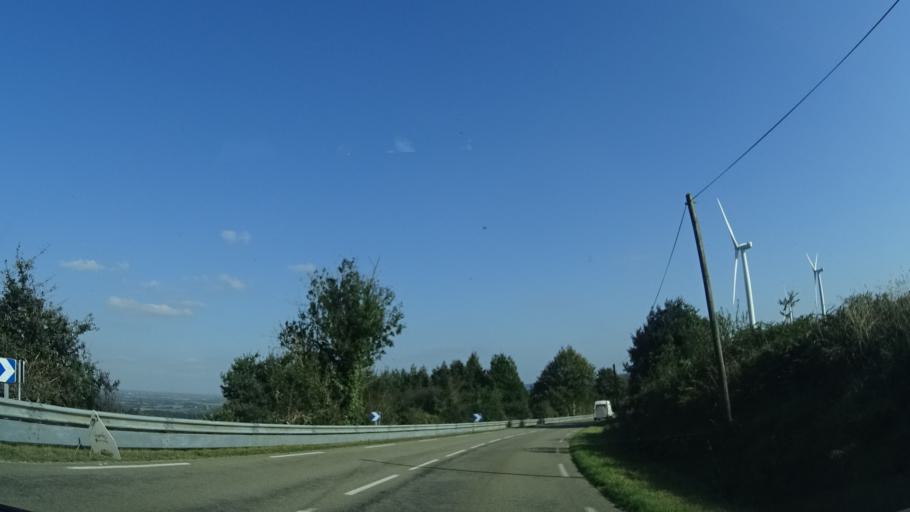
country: FR
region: Brittany
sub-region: Departement du Finistere
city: Cast
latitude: 48.1792
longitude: -4.1243
